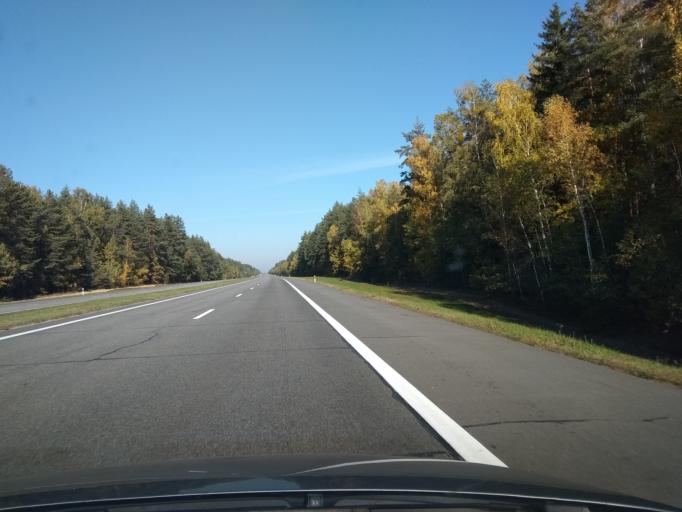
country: BY
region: Grodnenskaya
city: Zhyrovichy
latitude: 52.8646
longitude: 25.6541
